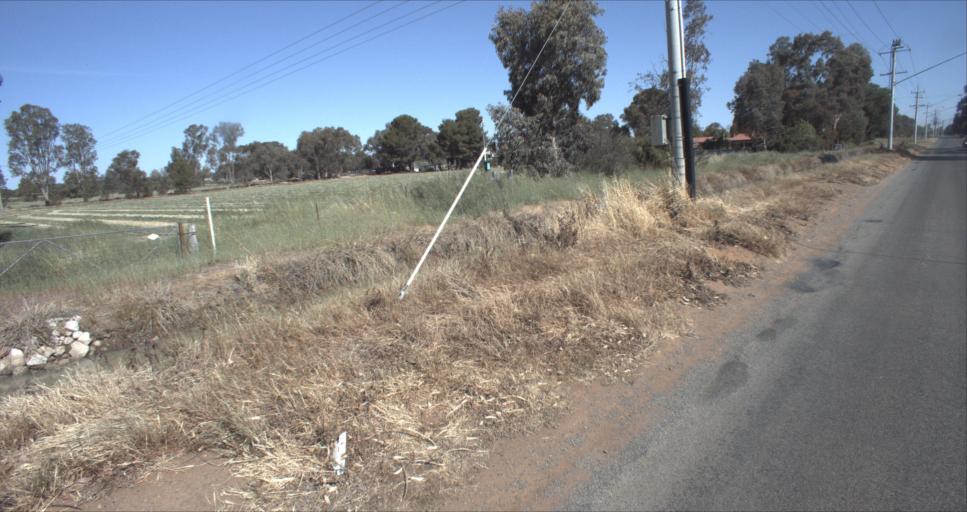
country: AU
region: New South Wales
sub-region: Leeton
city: Leeton
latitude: -34.5664
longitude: 146.4143
